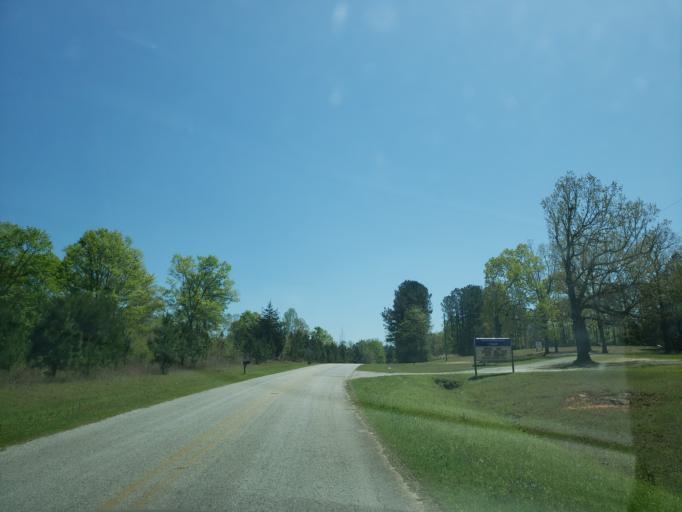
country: US
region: Alabama
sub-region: Tallapoosa County
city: Camp Hill
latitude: 32.6701
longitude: -85.7326
